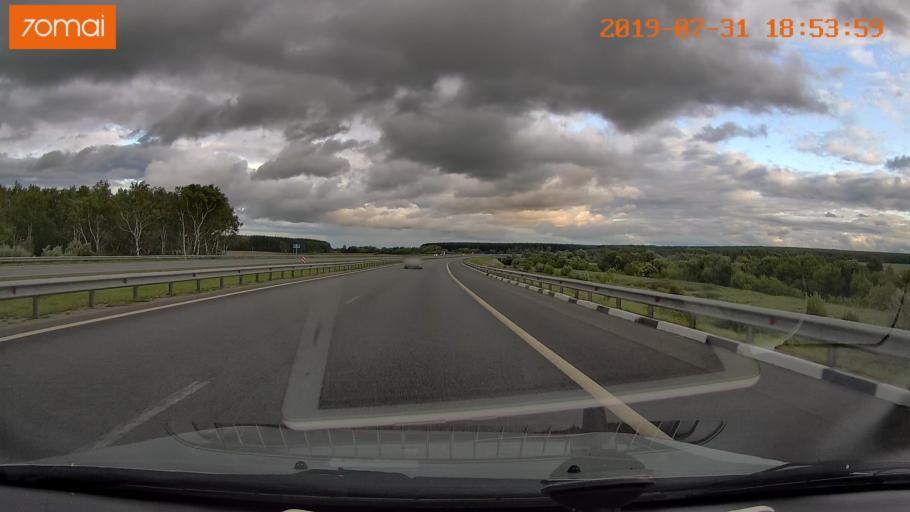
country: RU
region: Moskovskaya
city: Raduzhnyy
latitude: 55.1960
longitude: 38.6647
